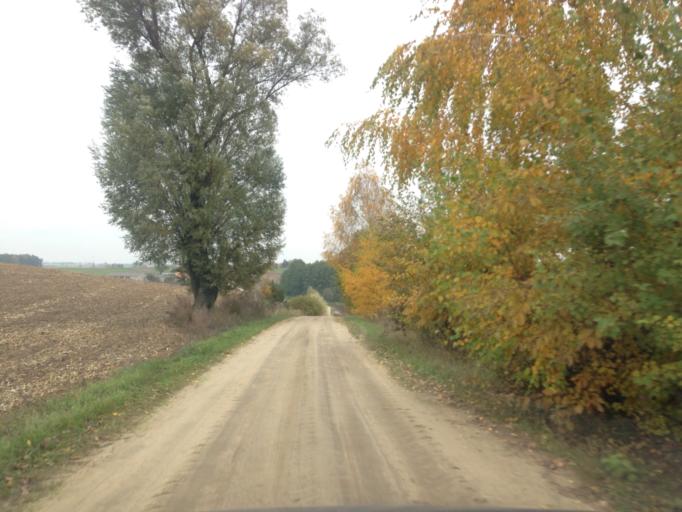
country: PL
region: Kujawsko-Pomorskie
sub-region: Powiat brodnicki
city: Brzozie
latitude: 53.3061
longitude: 19.6762
